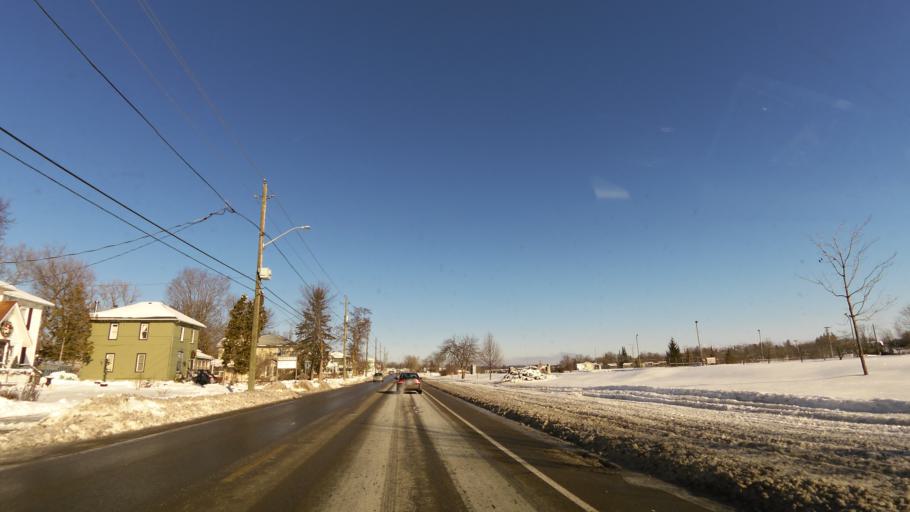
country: CA
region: Ontario
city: Quinte West
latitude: 44.3010
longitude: -77.8043
